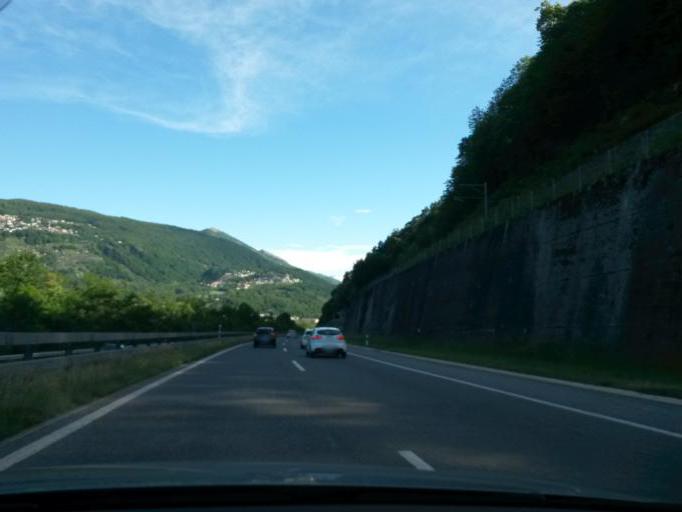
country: CH
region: Ticino
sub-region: Lugano District
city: Agno
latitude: 45.9984
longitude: 8.9158
